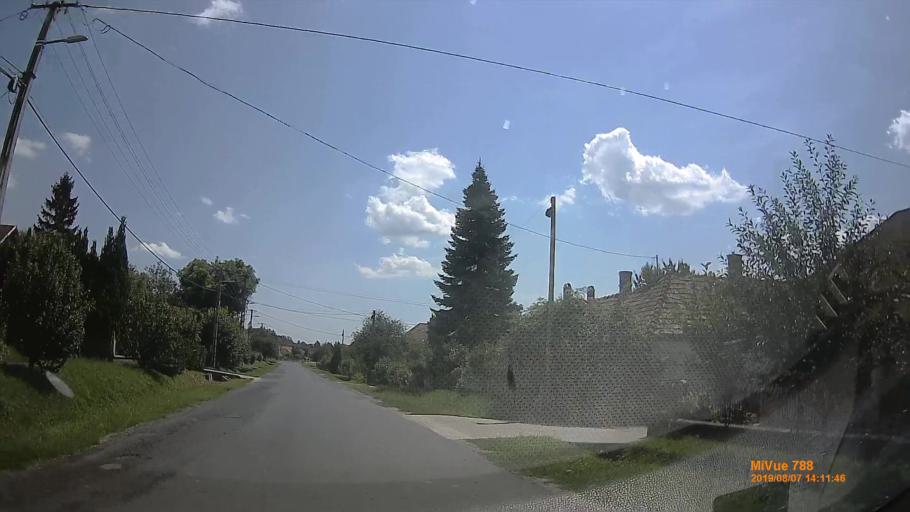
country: HU
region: Zala
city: Heviz
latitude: 46.8362
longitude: 17.1167
